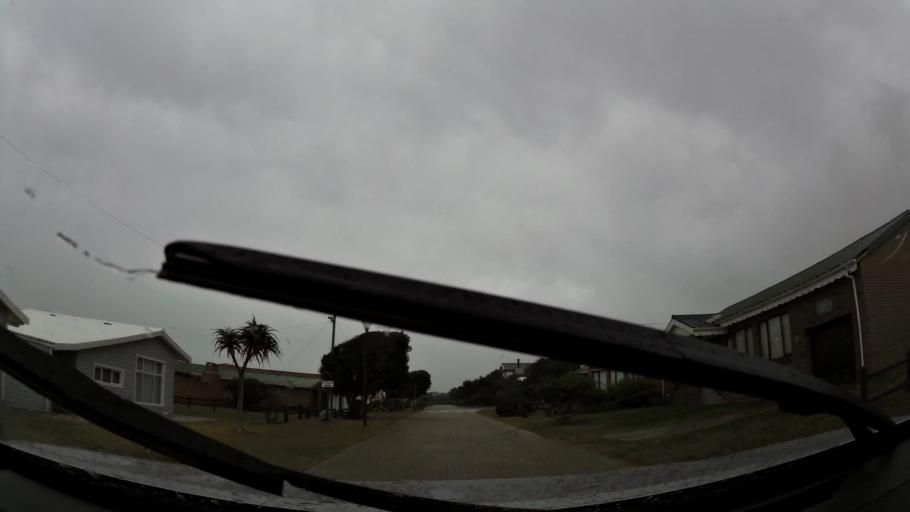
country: ZA
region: Western Cape
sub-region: Eden District Municipality
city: Mossel Bay
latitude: -34.0515
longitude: 22.2696
